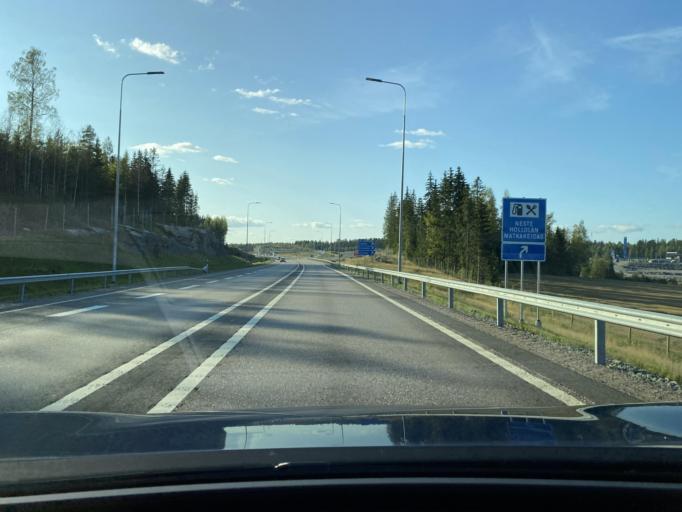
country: FI
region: Paijanne Tavastia
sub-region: Lahti
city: Hollola
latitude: 60.9770
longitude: 25.4988
